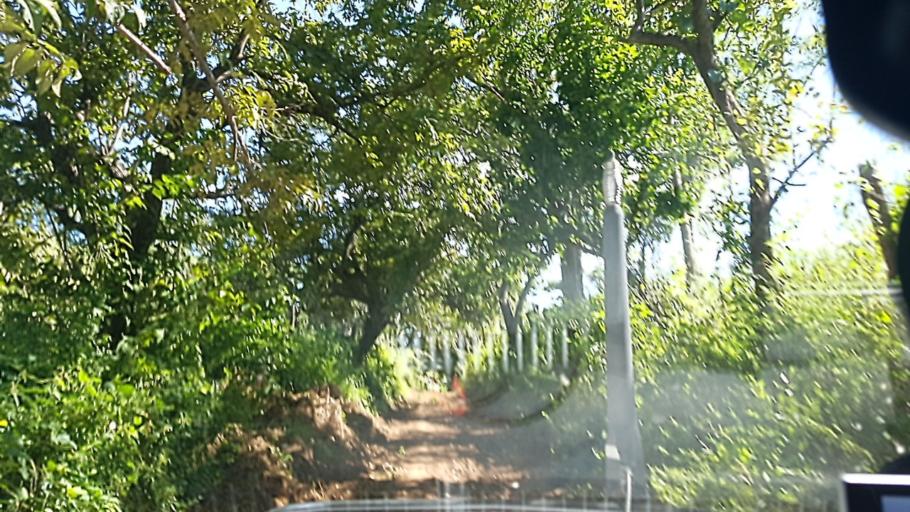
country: NI
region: Granada
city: Nandaime
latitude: 11.5736
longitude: -86.0931
